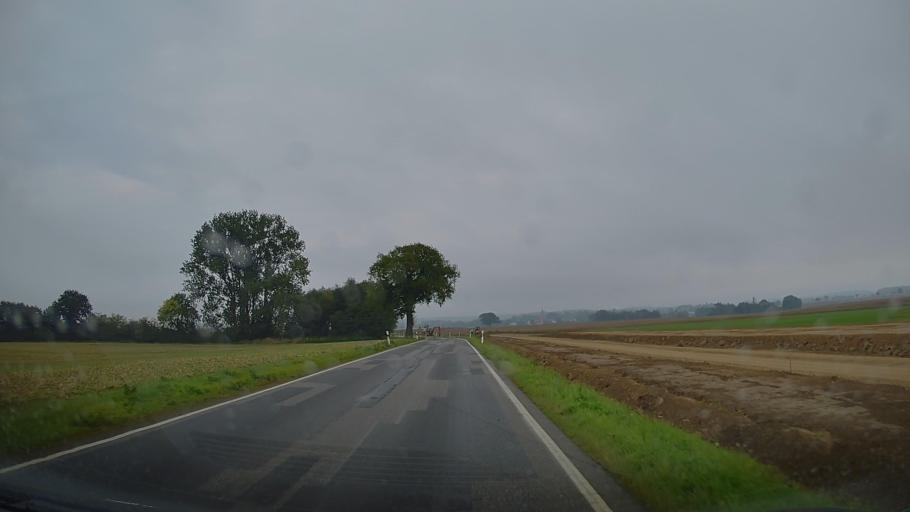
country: DE
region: Mecklenburg-Vorpommern
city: Kalkhorst
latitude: 53.9776
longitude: 11.0244
